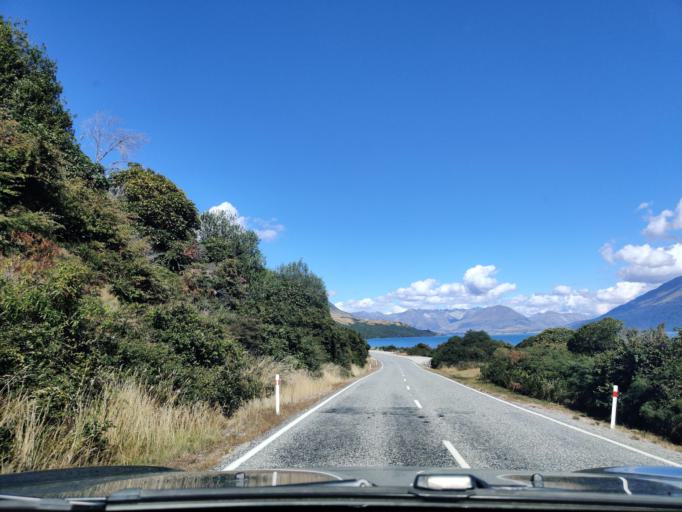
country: NZ
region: Otago
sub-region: Queenstown-Lakes District
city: Queenstown
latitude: -44.9446
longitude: 168.4331
